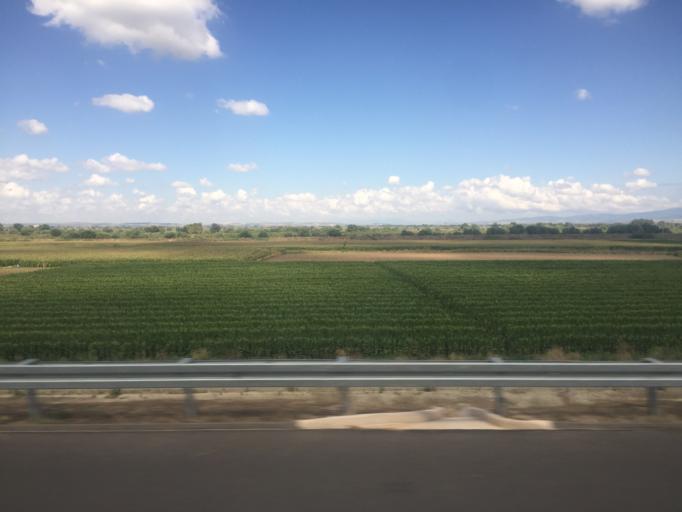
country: TR
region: Bursa
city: Karacabey
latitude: 40.1326
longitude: 28.2924
